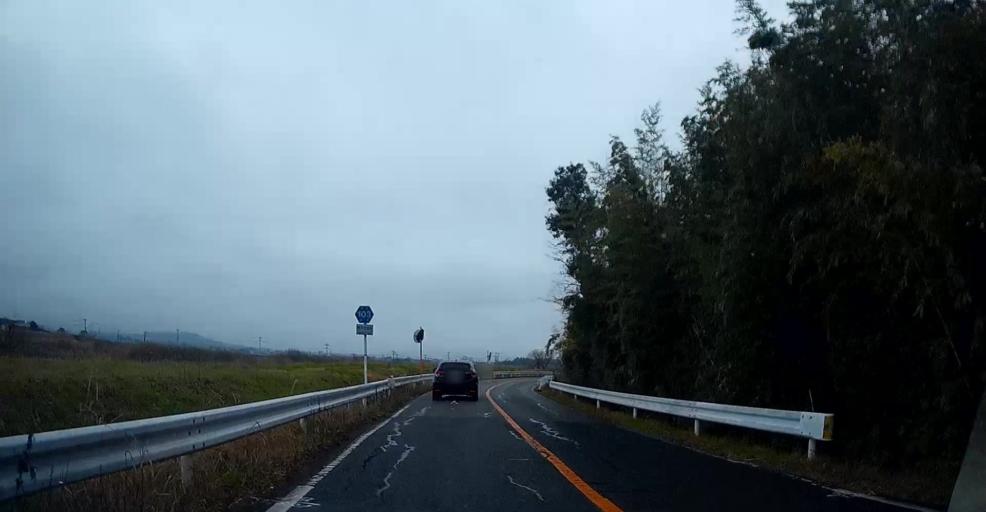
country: JP
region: Kumamoto
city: Kumamoto
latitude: 32.7557
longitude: 130.7486
